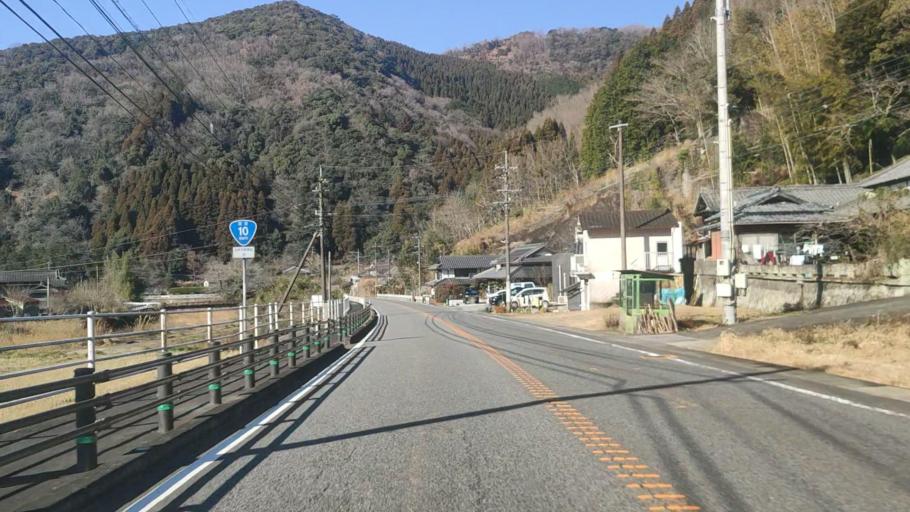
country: JP
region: Oita
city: Usuki
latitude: 33.0052
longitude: 131.7419
